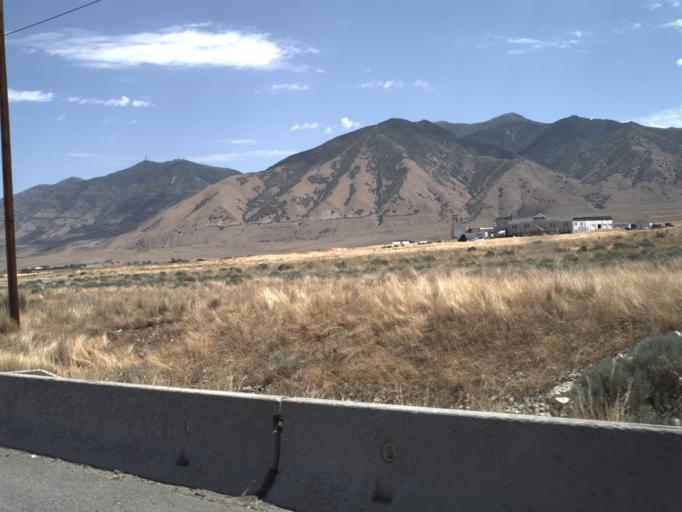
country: US
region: Utah
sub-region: Tooele County
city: Tooele
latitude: 40.5638
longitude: -112.2961
